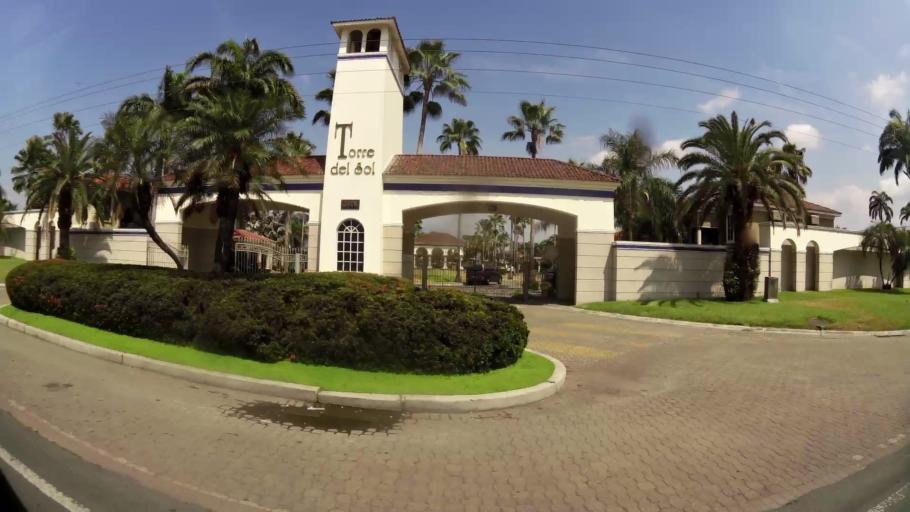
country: EC
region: Guayas
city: Eloy Alfaro
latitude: -2.1212
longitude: -79.8660
